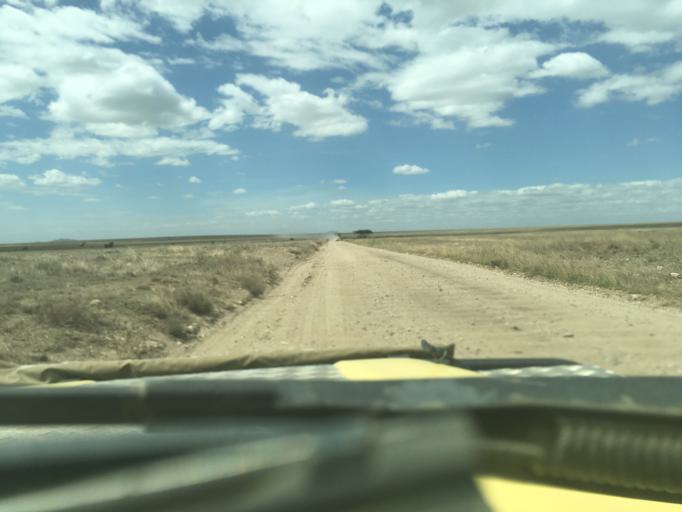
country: TZ
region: Mara
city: Mugumu
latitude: -2.5947
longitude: 34.8825
